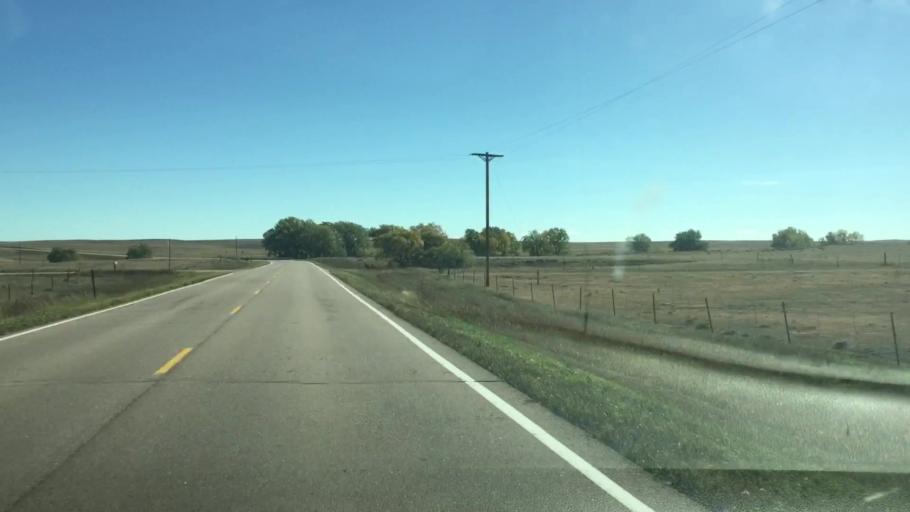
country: US
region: Colorado
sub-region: Lincoln County
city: Limon
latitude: 39.2735
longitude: -104.0132
